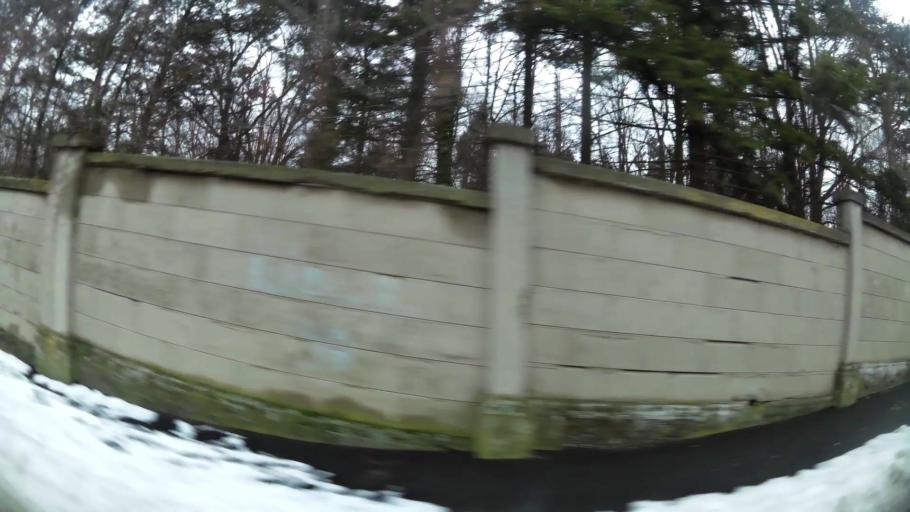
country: RS
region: Central Serbia
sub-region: Belgrade
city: Savski Venac
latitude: 44.7641
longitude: 20.4542
